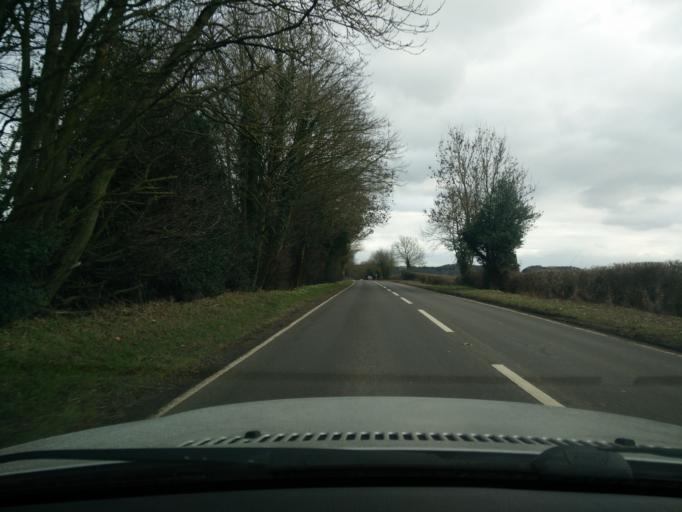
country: GB
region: England
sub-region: Buckinghamshire
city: Amersham
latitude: 51.6581
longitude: -0.6581
